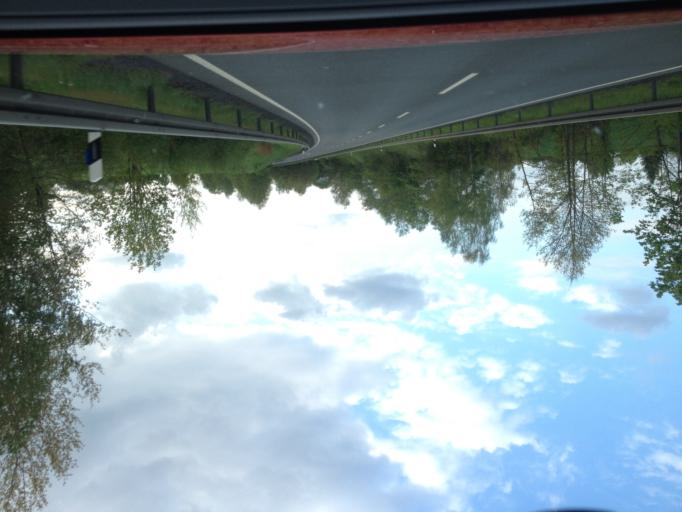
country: DE
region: Bavaria
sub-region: Upper Franconia
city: Arzberg
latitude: 50.0390
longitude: 12.1596
